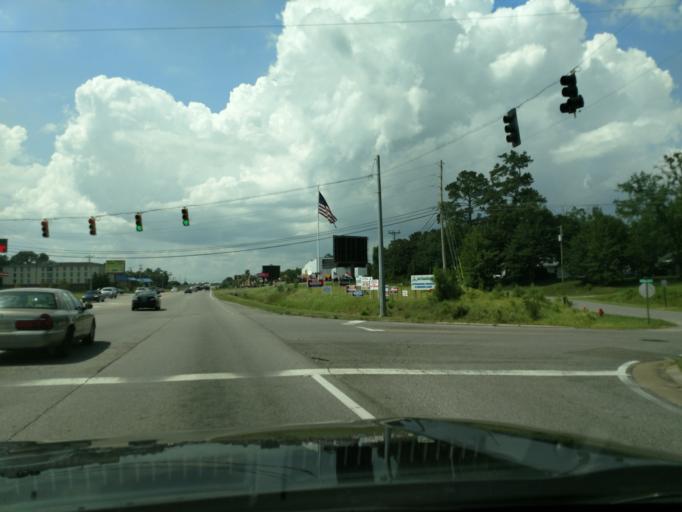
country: US
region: Mississippi
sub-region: Jackson County
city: Gulf Hills
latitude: 30.4442
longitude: -88.8391
